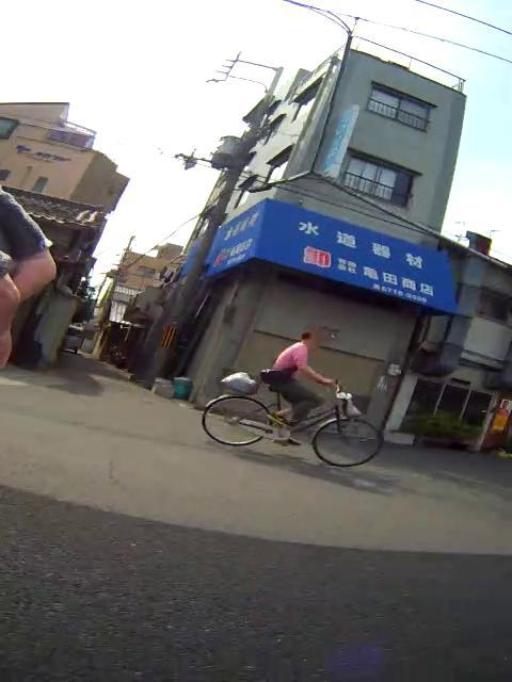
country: JP
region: Osaka
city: Osaka-shi
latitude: 34.6603
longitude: 135.5417
